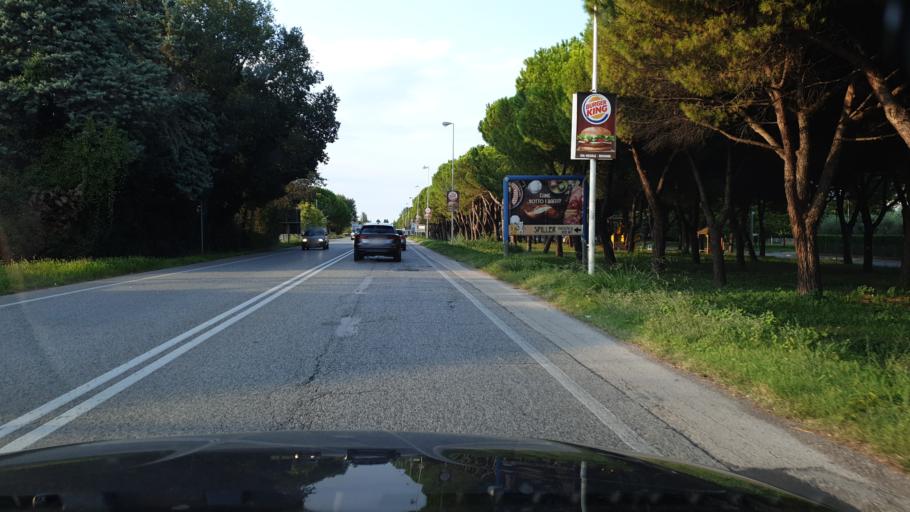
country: IT
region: Emilia-Romagna
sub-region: Provincia di Rimini
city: Riccione
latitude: 44.0061
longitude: 12.6337
